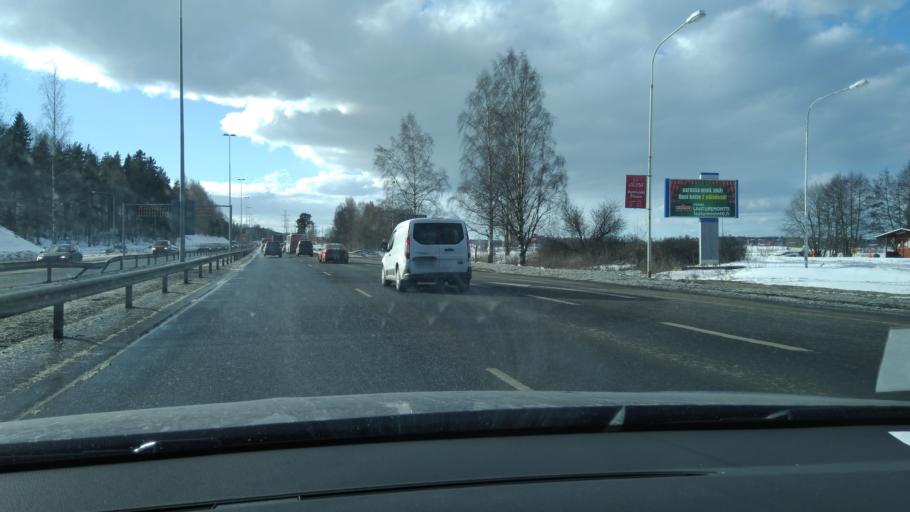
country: FI
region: Pirkanmaa
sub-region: Tampere
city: Tampere
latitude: 61.5067
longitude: 23.7116
